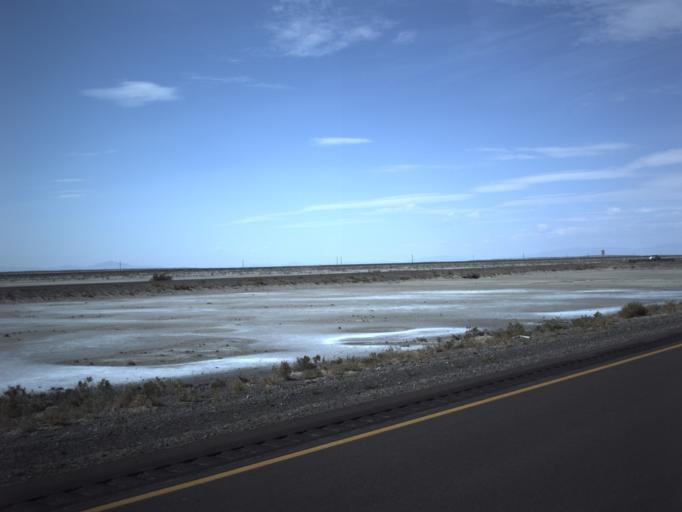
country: US
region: Utah
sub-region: Tooele County
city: Wendover
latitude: 40.7282
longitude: -113.3100
